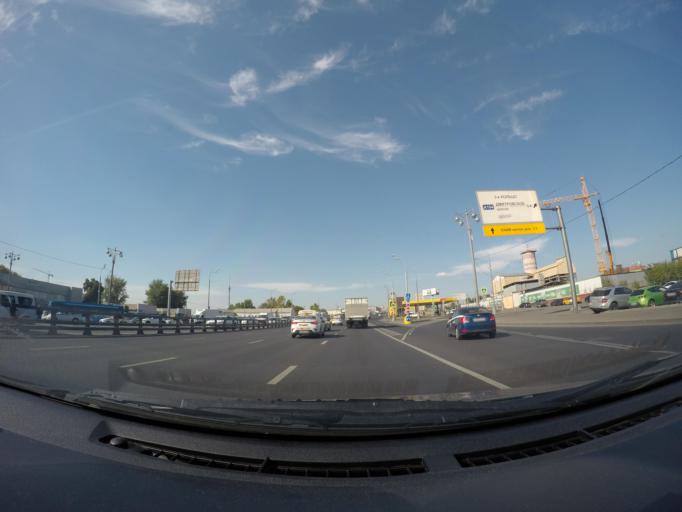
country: RU
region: Moscow
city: Mar'ina Roshcha
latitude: 55.7937
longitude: 37.6347
